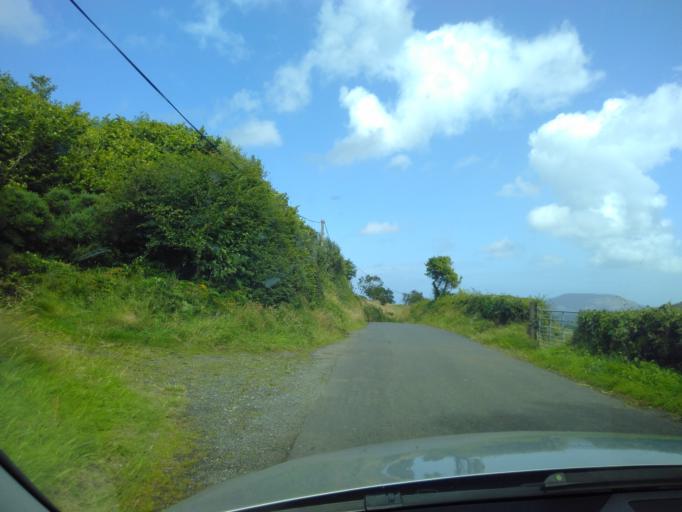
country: IE
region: Ulster
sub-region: County Donegal
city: Ramelton
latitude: 55.2270
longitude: -7.6222
